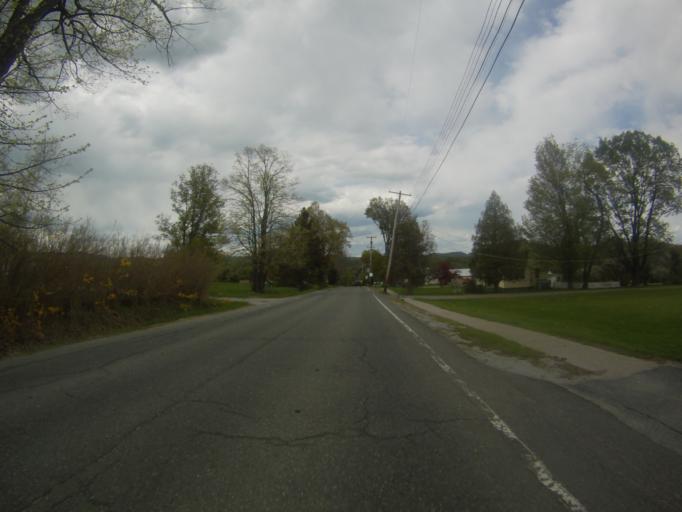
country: US
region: New York
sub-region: Essex County
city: Mineville
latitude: 44.0563
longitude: -73.5084
